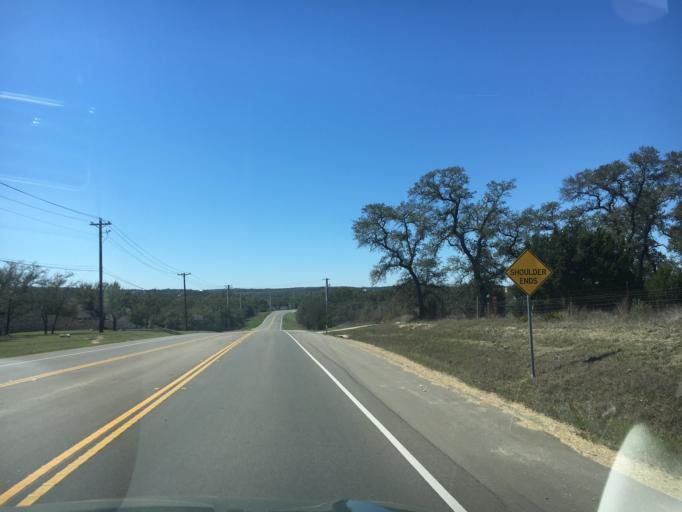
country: US
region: Texas
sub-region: Travis County
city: The Hills
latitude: 30.2917
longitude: -98.0347
